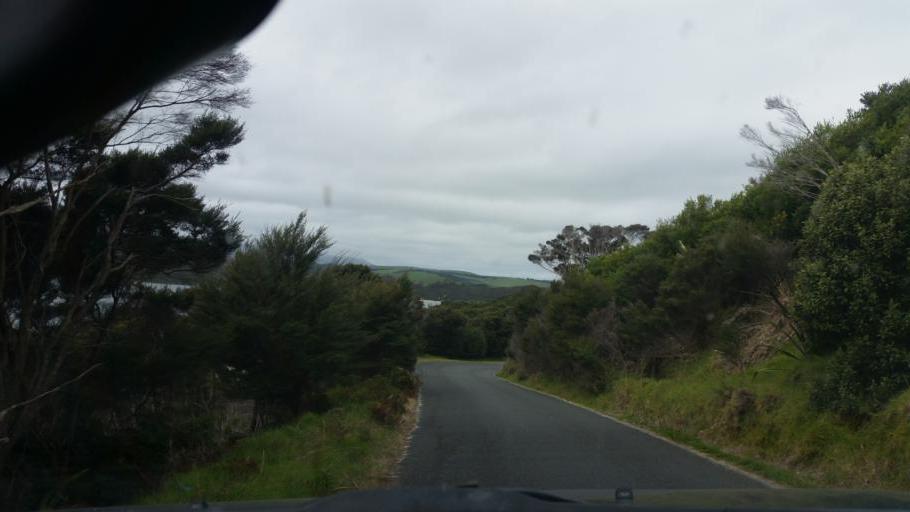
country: NZ
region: Northland
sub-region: Kaipara District
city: Dargaville
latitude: -35.8129
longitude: 173.6453
